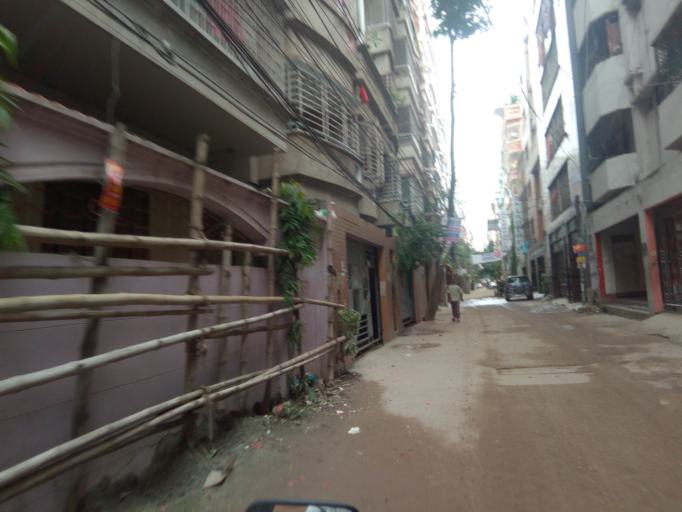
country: BD
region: Dhaka
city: Paltan
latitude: 23.7630
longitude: 90.4280
